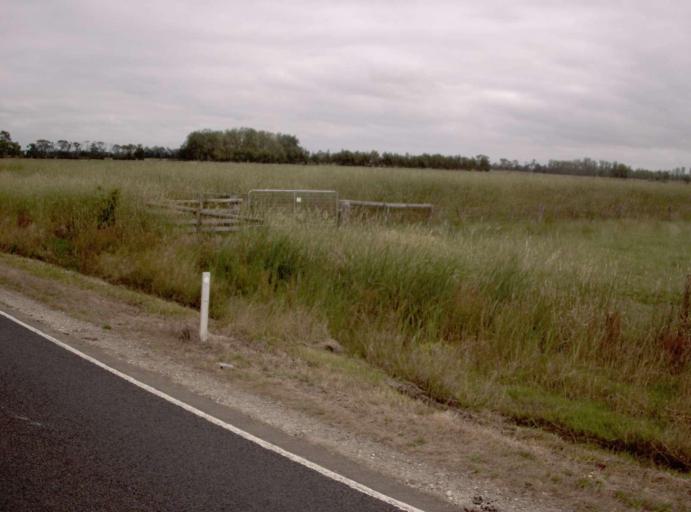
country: AU
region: Victoria
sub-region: Wellington
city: Sale
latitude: -38.0492
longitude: 146.9516
